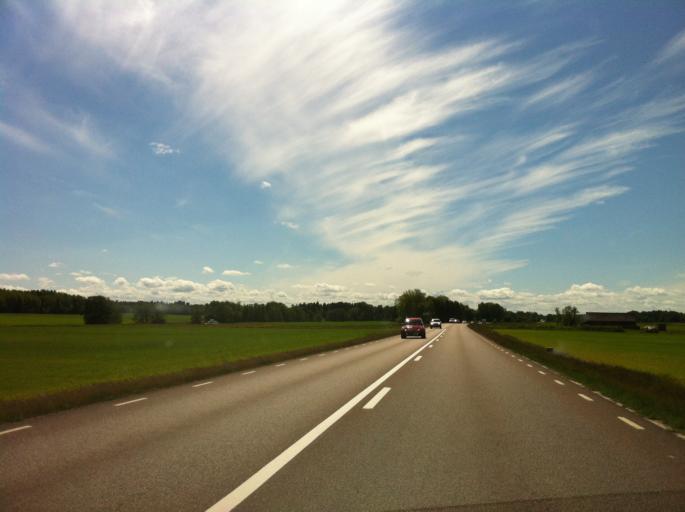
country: SE
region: Vaestra Goetaland
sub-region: Vanersborgs Kommun
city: Bralanda
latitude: 58.5214
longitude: 12.3071
